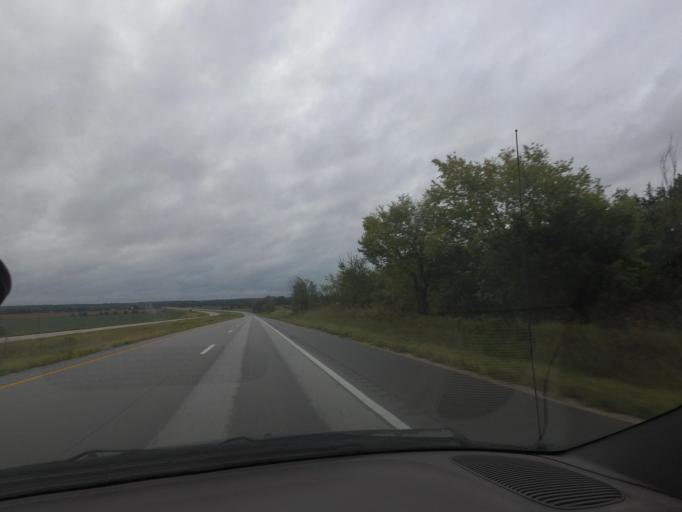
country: US
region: Missouri
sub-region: Shelby County
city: Shelbina
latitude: 39.6677
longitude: -91.9293
